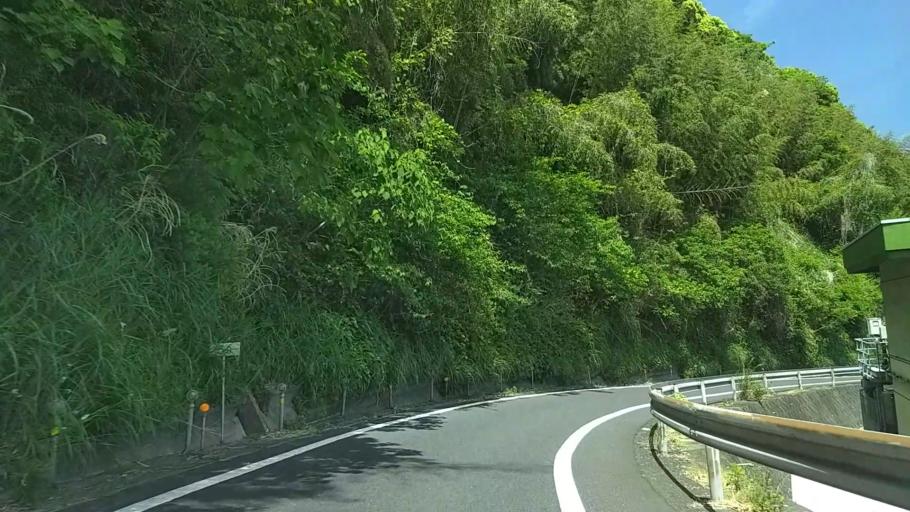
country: JP
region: Kanagawa
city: Yugawara
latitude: 35.1700
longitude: 139.1426
